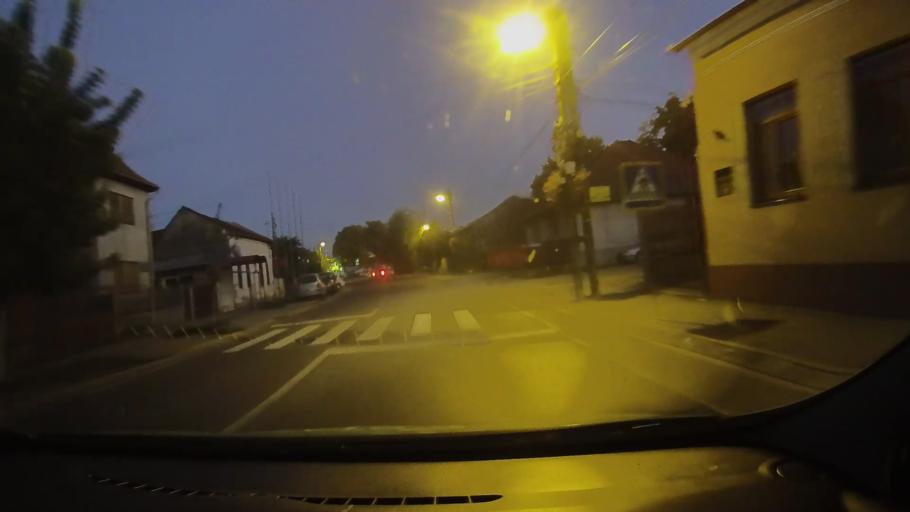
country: RO
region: Bihor
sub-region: Comuna Valea lui Mihai
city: Valea lui Mihai
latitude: 47.5155
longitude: 22.1360
